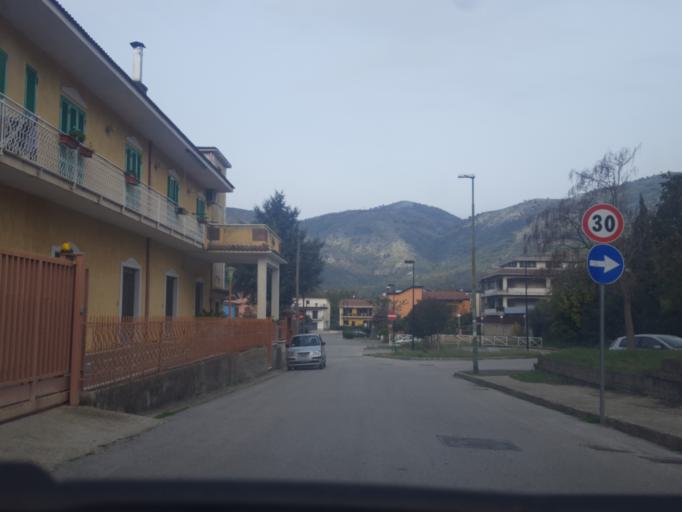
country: IT
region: Campania
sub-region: Provincia di Caserta
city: Arienzo
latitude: 41.0235
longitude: 14.4972
